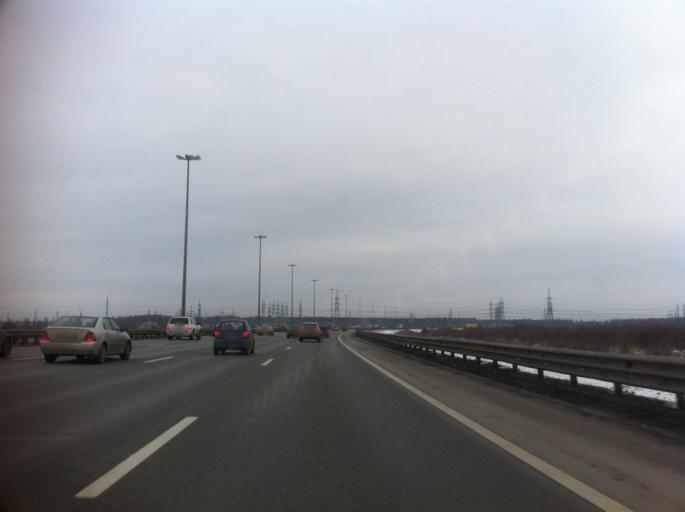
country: RU
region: Leningrad
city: Rybatskoye
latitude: 59.8995
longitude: 30.5260
